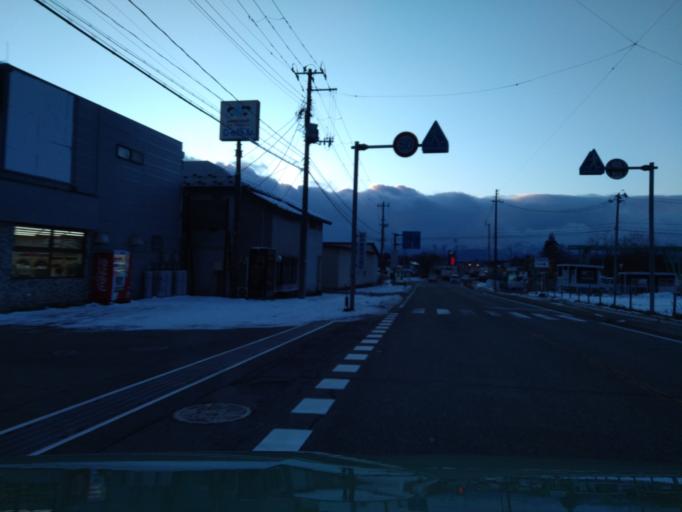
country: JP
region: Iwate
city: Shizukuishi
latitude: 39.6891
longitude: 140.9985
